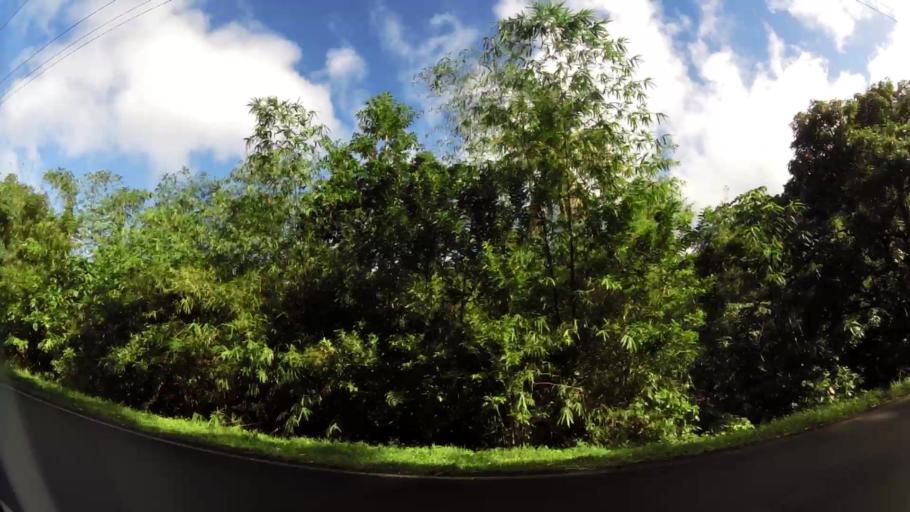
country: LC
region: Soufriere
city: Soufriere
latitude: 13.8685
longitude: -61.0477
